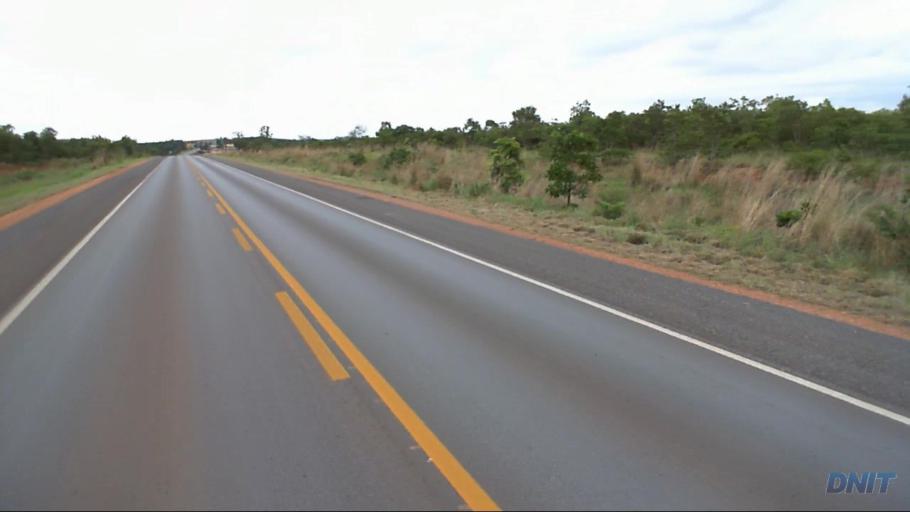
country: BR
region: Goias
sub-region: Barro Alto
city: Barro Alto
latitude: -15.2091
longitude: -48.6884
